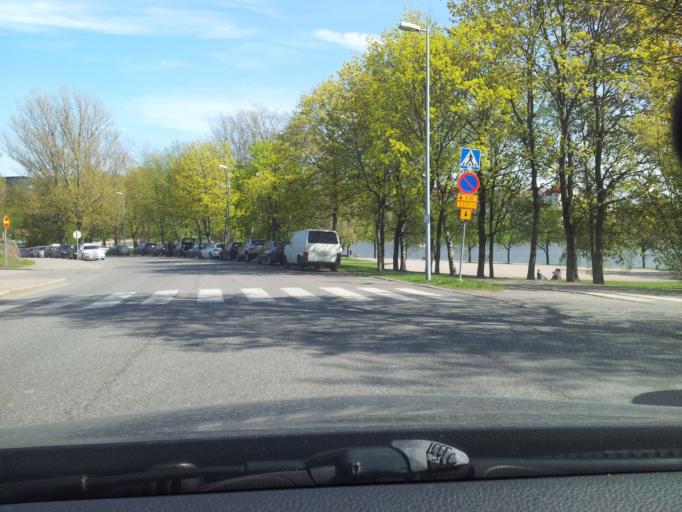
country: FI
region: Uusimaa
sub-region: Helsinki
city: Helsinki
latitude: 60.1810
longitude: 24.9416
